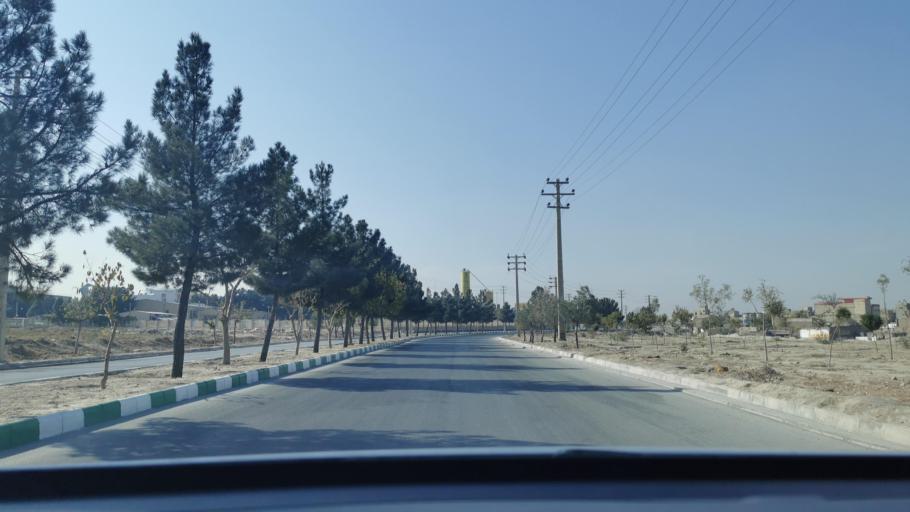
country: IR
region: Razavi Khorasan
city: Mashhad
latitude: 36.3480
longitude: 59.6047
